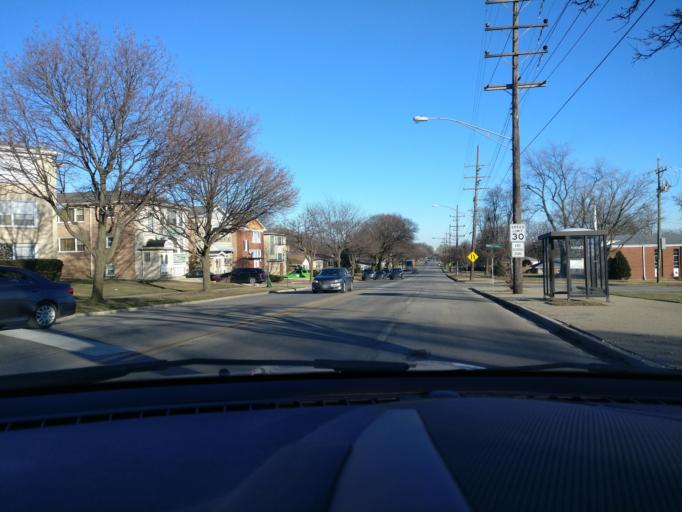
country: US
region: Illinois
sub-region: Cook County
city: Skokie
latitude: 42.0480
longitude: -87.7428
